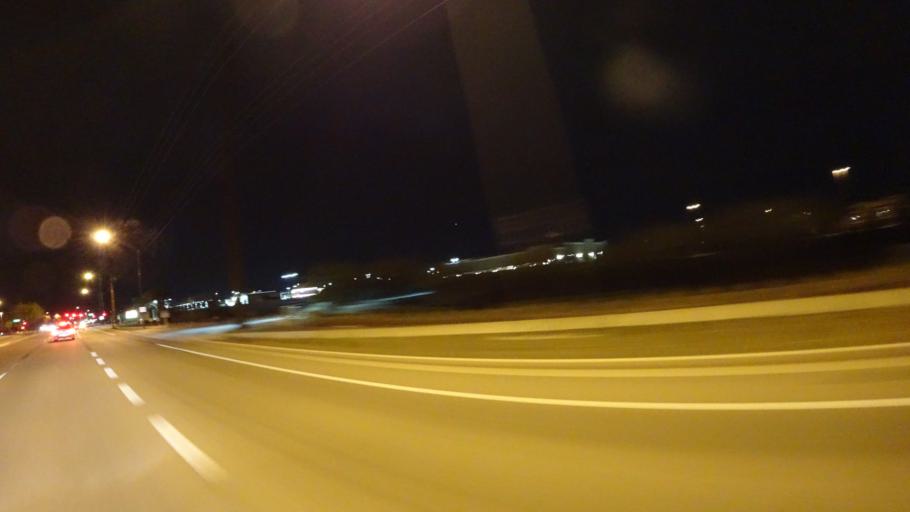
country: US
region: Arizona
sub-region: Maricopa County
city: Gilbert
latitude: 33.2923
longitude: -111.7238
